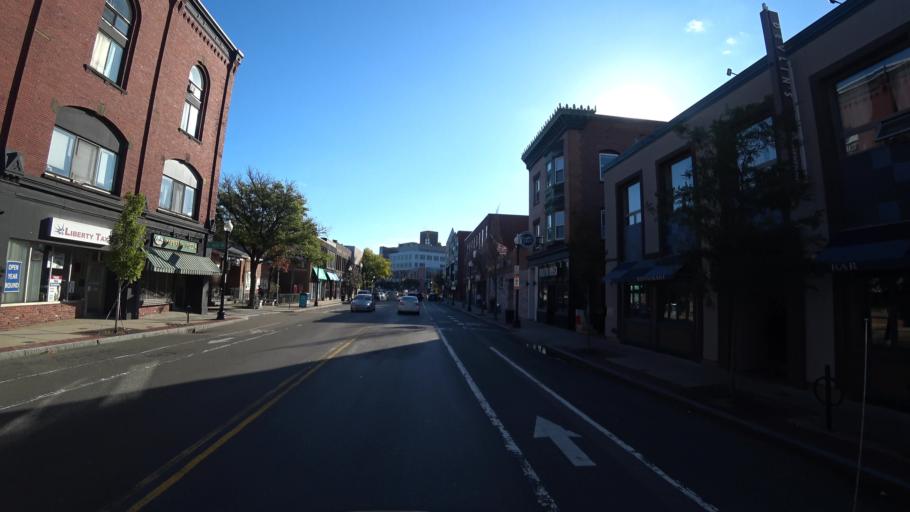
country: US
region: Massachusetts
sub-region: Norfolk County
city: Brookline
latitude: 42.3490
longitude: -71.1525
